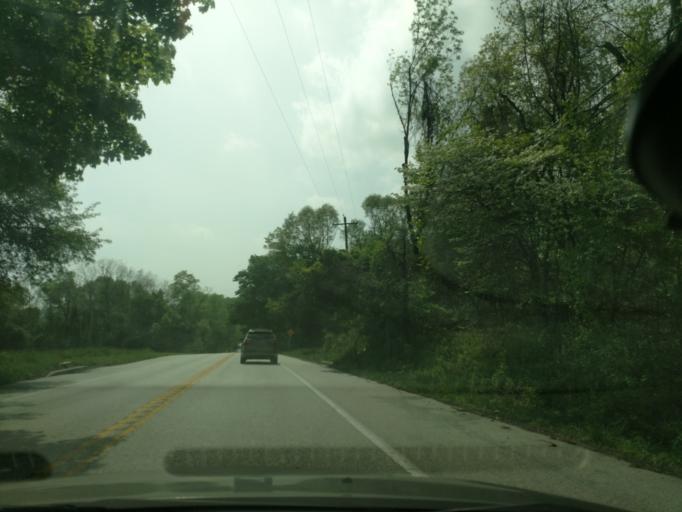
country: US
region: Pennsylvania
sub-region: Montgomery County
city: Stowe
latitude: 40.1754
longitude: -75.7145
